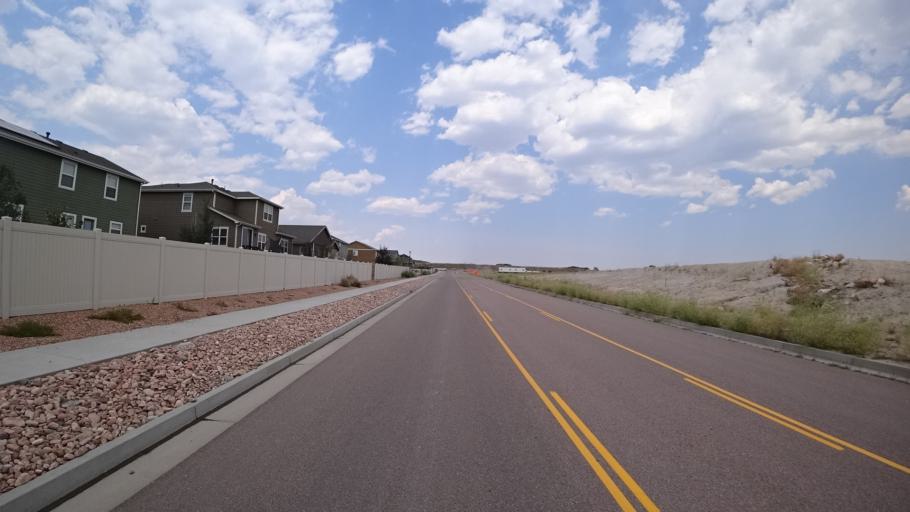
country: US
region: Colorado
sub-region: El Paso County
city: Black Forest
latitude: 38.9458
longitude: -104.6843
